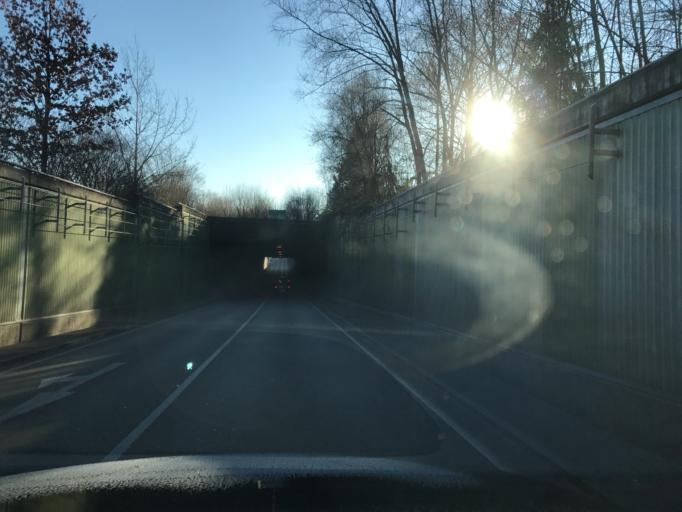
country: DE
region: Bavaria
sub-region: Upper Bavaria
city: Bad Aibling
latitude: 47.8576
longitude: 11.9899
